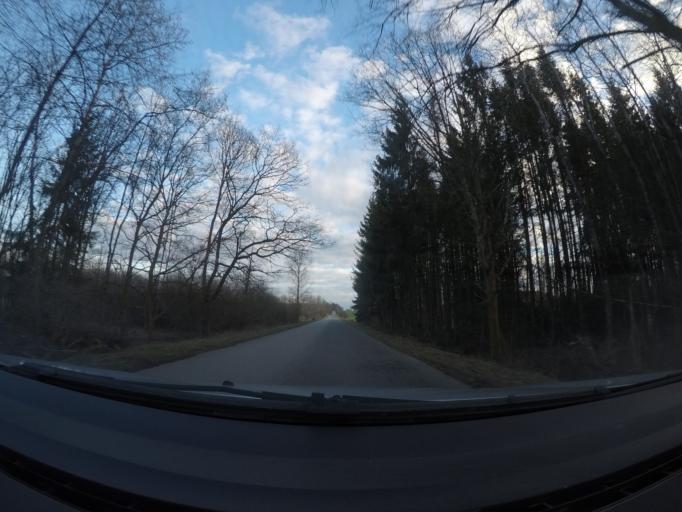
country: BE
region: Wallonia
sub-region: Province du Luxembourg
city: Etalle
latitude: 49.6874
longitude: 5.5629
